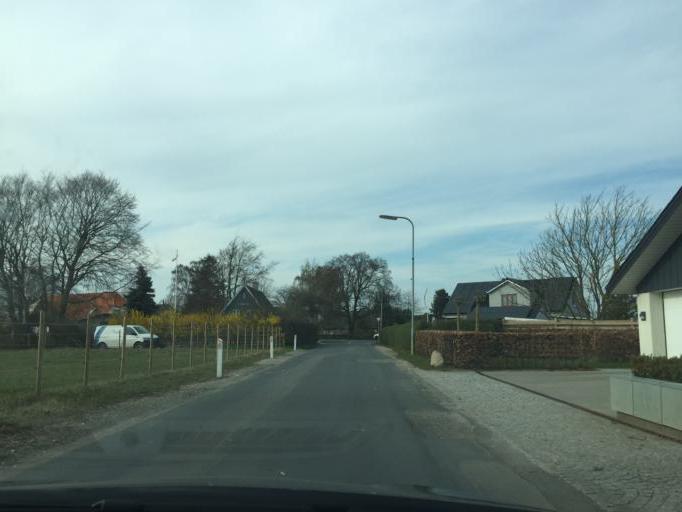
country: DK
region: South Denmark
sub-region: Faaborg-Midtfyn Kommune
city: Arslev
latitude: 55.3337
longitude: 10.5108
